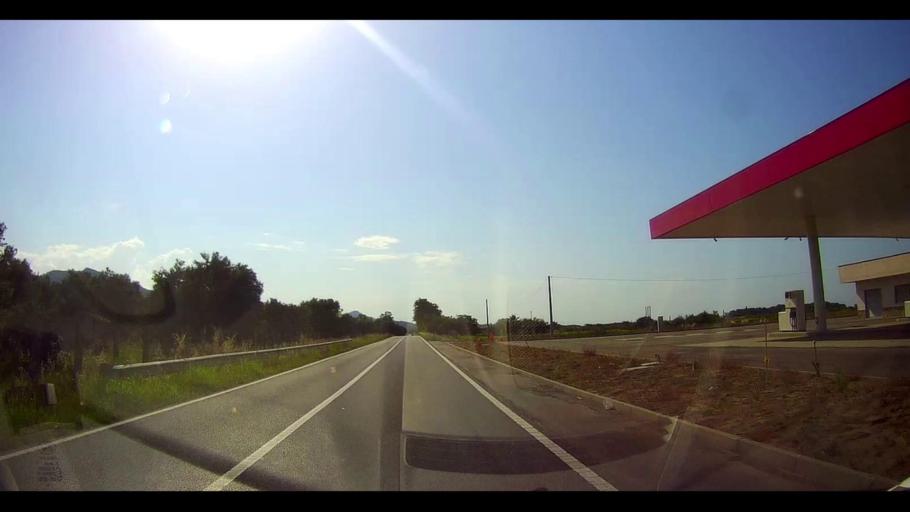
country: IT
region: Calabria
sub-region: Provincia di Cosenza
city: Cariati
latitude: 39.4792
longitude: 16.9942
